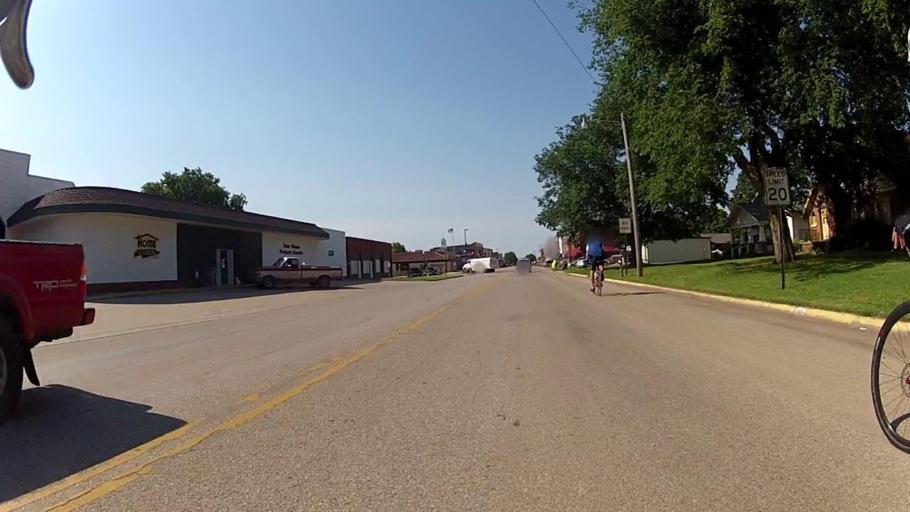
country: US
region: Kansas
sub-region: Sumner County
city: Caldwell
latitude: 37.0342
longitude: -97.6070
